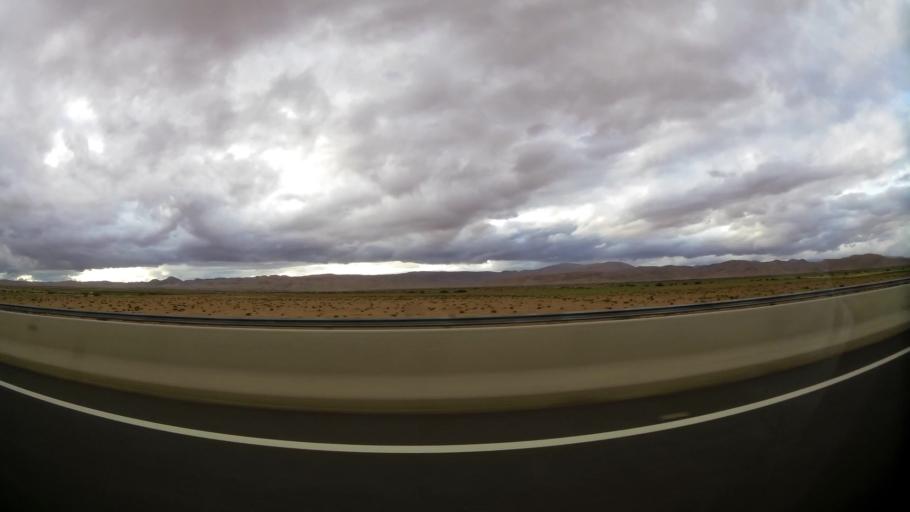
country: MA
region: Taza-Al Hoceima-Taounate
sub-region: Taza
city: Guercif
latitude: 34.3138
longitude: -3.5951
